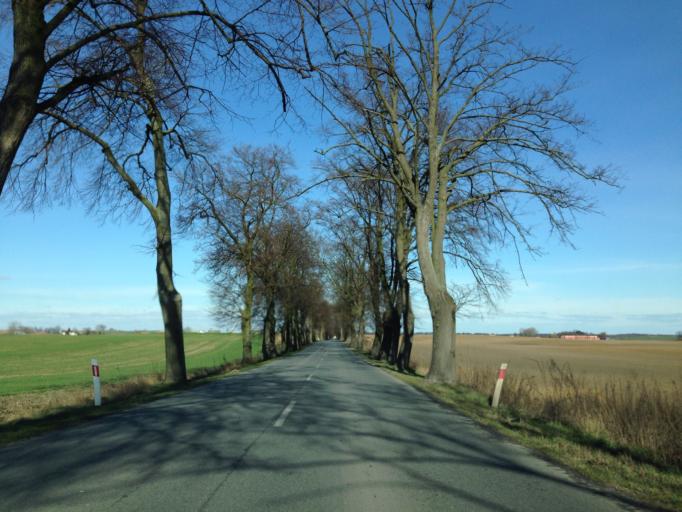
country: PL
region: Pomeranian Voivodeship
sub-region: Powiat sztumski
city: Stary Targ
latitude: 53.9844
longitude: 19.1163
